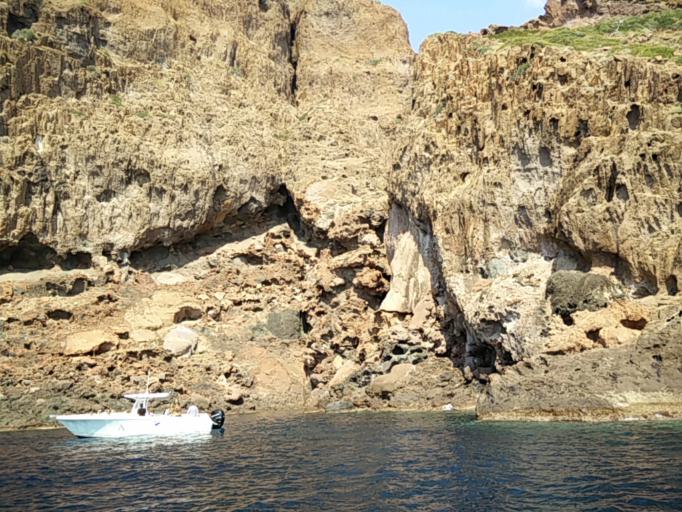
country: FR
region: Corsica
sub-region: Departement de la Corse-du-Sud
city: Cargese
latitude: 42.3457
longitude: 8.5539
